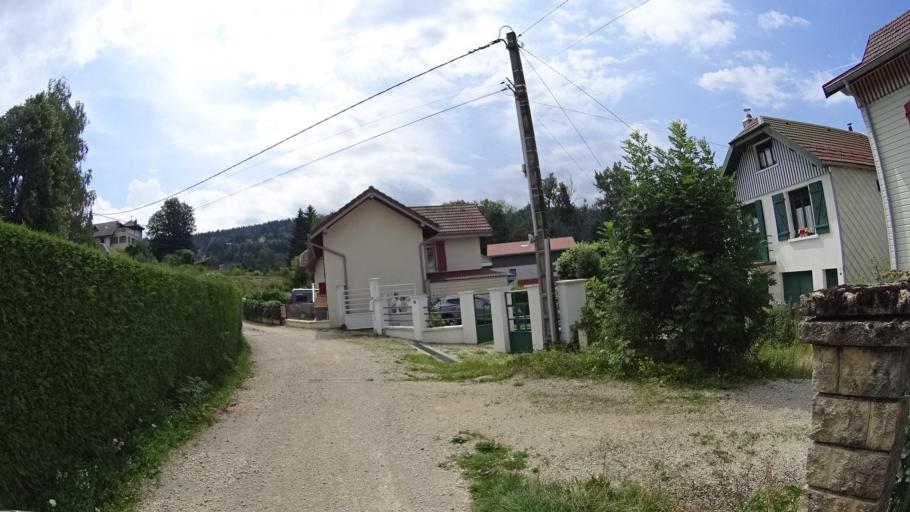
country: FR
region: Franche-Comte
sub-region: Departement du Doubs
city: Les Fourgs
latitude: 46.8368
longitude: 6.3399
